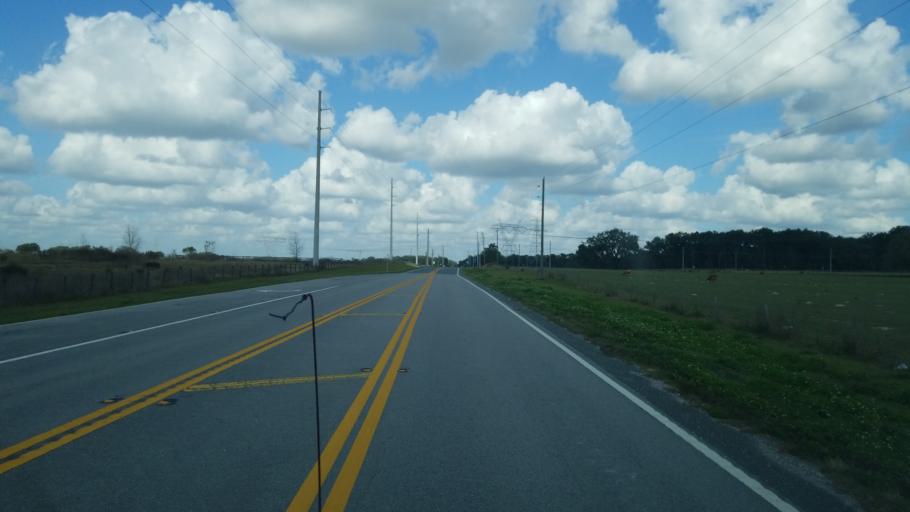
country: US
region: Florida
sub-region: Sumter County
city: Wildwood
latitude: 28.8911
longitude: -82.1200
